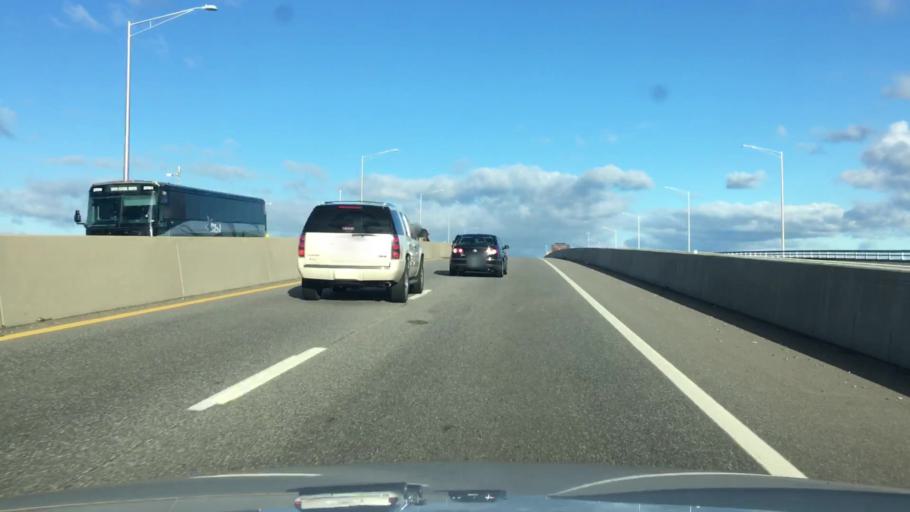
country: US
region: Maine
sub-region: York County
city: Eliot
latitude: 43.1172
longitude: -70.8245
